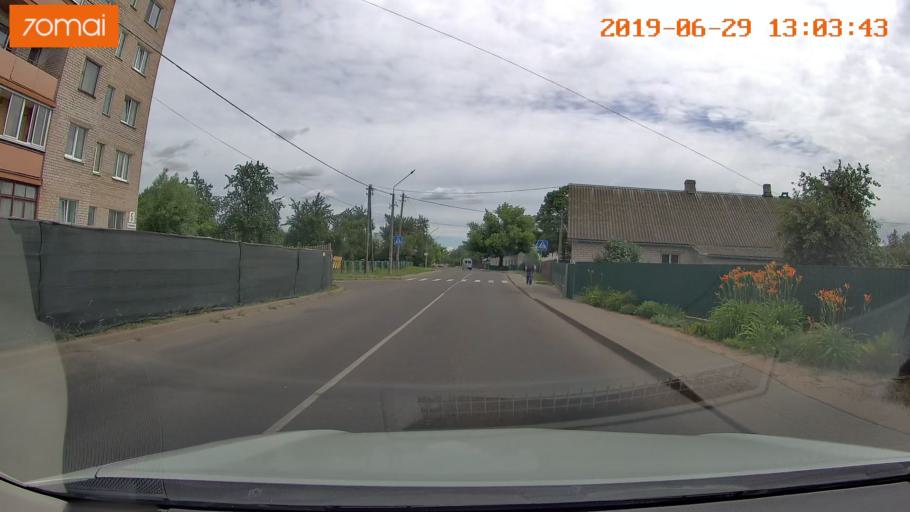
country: BY
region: Minsk
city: Slutsk
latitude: 53.0313
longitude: 27.5634
